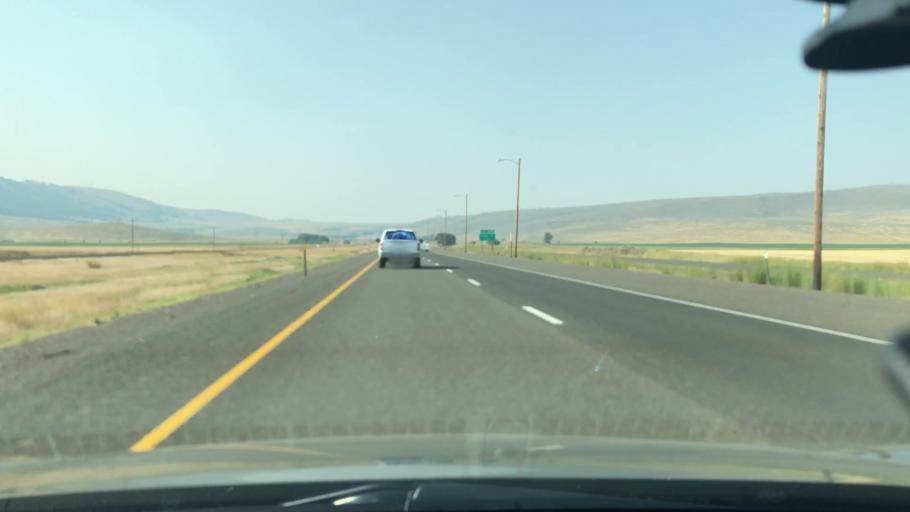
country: US
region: Oregon
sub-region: Union County
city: Union
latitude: 45.1065
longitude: -117.9561
